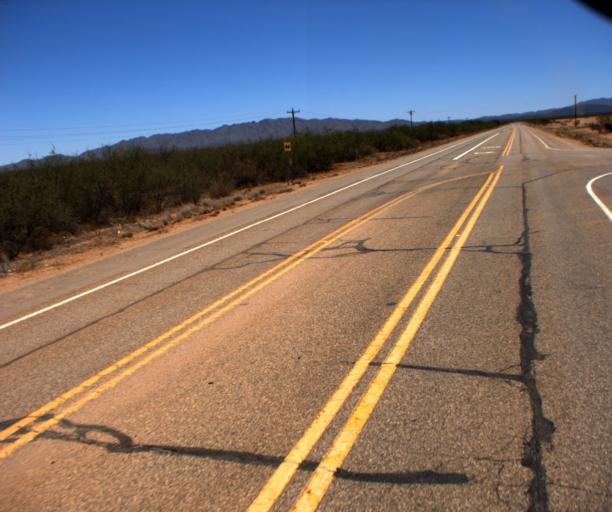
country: US
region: Arizona
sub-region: Pima County
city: Ajo
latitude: 32.1850
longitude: -112.3684
